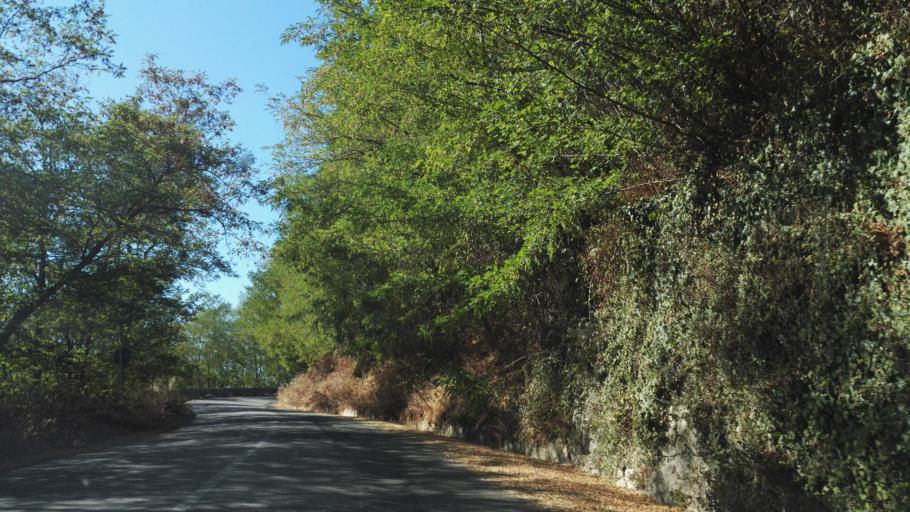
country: IT
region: Calabria
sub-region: Provincia di Vibo-Valentia
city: Sorianello
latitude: 38.5900
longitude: 16.2401
